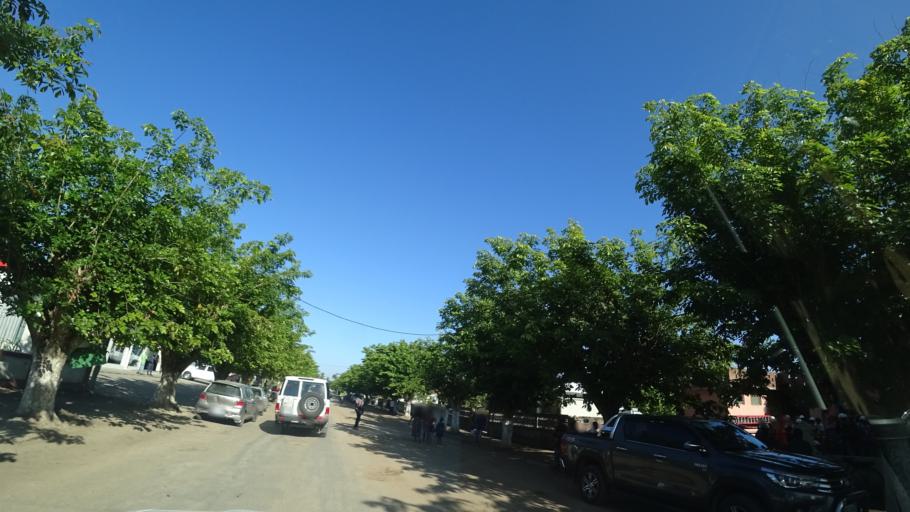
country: MZ
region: Sofala
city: Dondo
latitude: -19.6159
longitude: 34.7441
